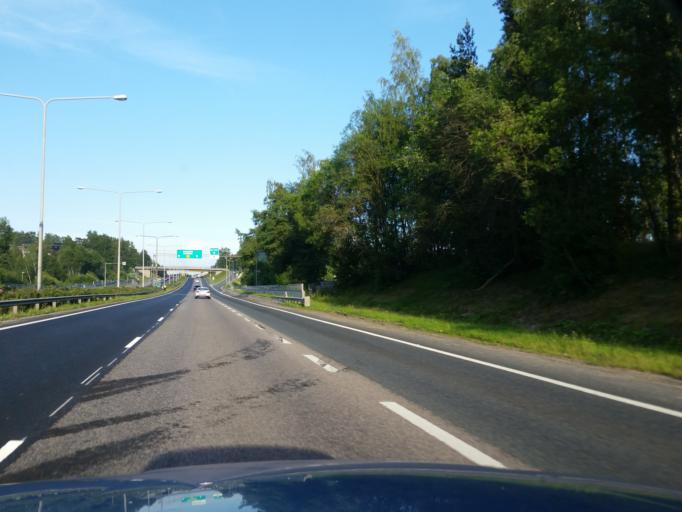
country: FI
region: Uusimaa
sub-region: Helsinki
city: Teekkarikylae
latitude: 60.1646
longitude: 24.8499
